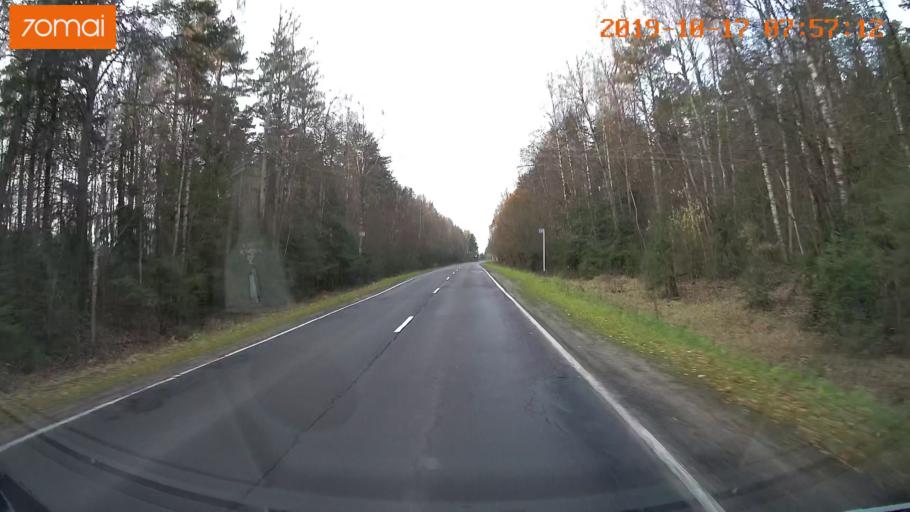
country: RU
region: Vladimir
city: Bavleny
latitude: 56.4140
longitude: 39.5806
